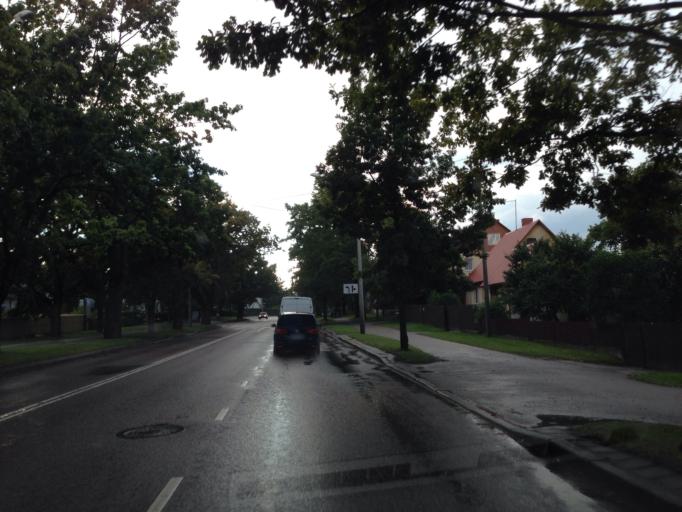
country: EE
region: Tartu
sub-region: Tartu linn
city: Tartu
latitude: 58.3650
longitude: 26.7005
